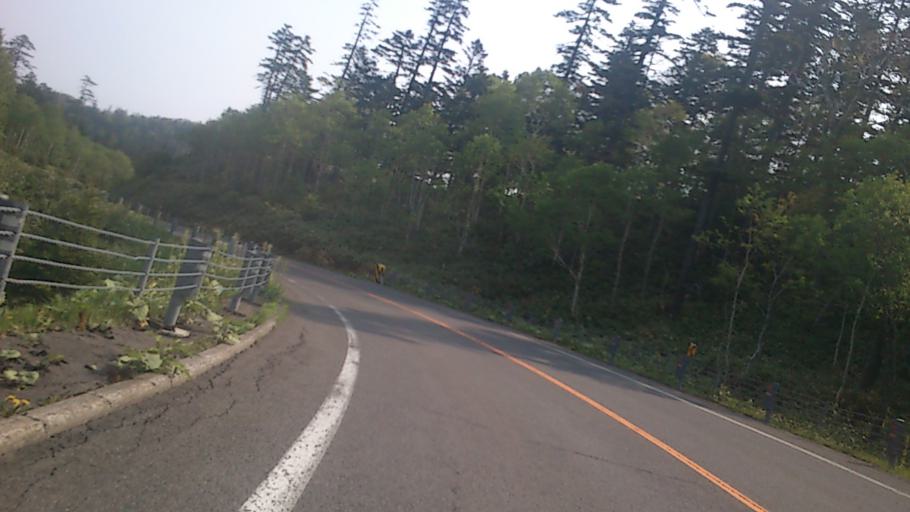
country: JP
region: Hokkaido
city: Bihoro
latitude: 43.4572
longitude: 144.2232
